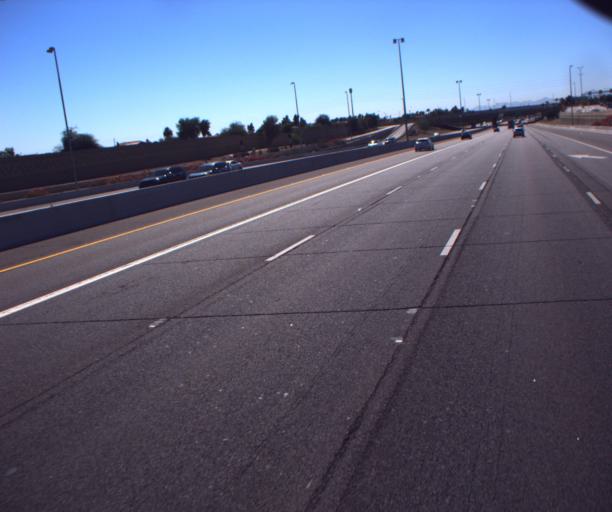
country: US
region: Arizona
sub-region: Maricopa County
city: Sun City
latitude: 33.6566
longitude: -112.2326
